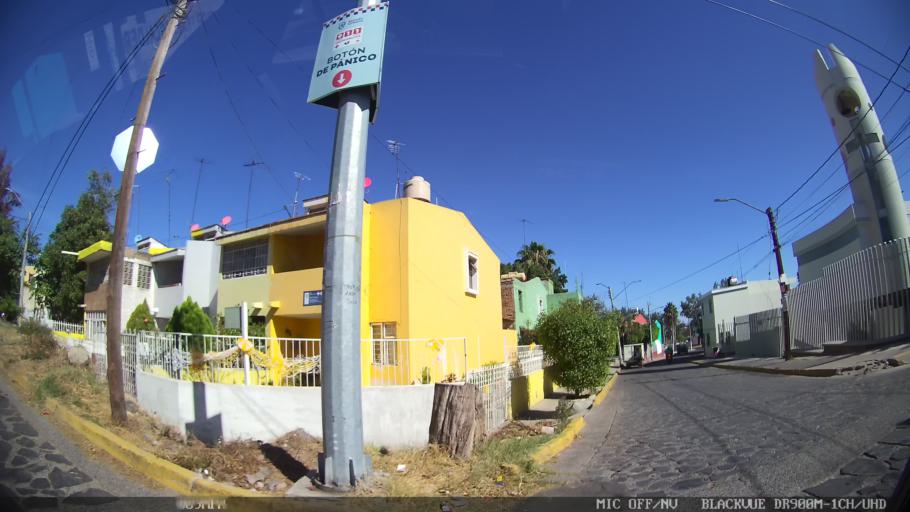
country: MX
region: Jalisco
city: Tlaquepaque
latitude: 20.6816
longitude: -103.2695
